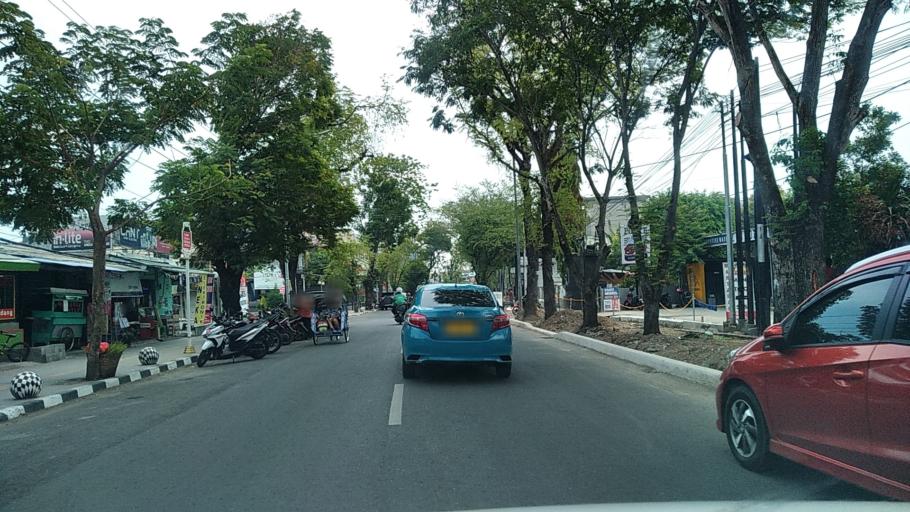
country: ID
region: Central Java
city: Semarang
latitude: -6.9799
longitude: 110.4040
